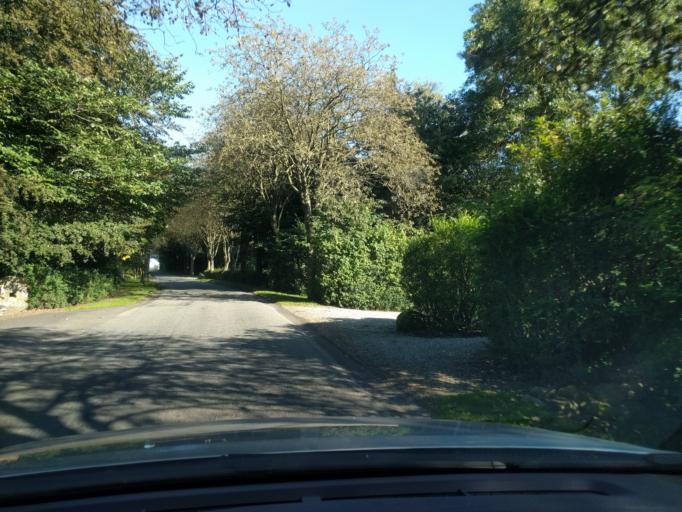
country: DK
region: Central Jutland
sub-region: Horsens Kommune
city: Horsens
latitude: 55.9245
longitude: 9.8603
